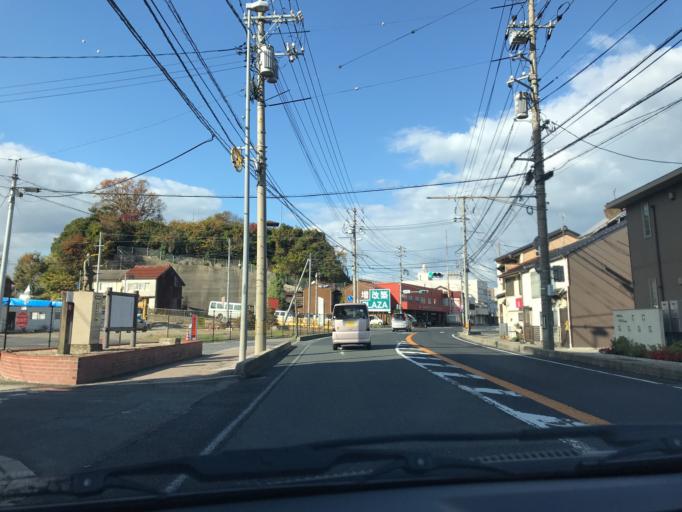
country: JP
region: Shimane
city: Yasugicho
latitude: 35.4287
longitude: 133.2580
